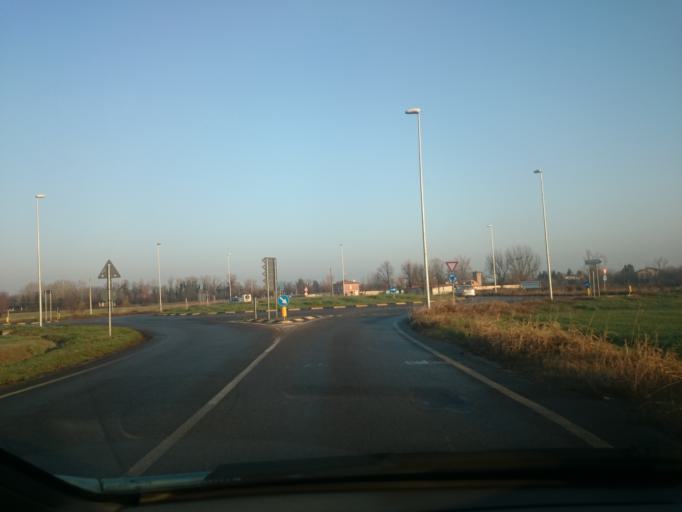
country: IT
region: Emilia-Romagna
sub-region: Provincia di Reggio Emilia
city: Fellegara
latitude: 44.6044
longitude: 10.7045
